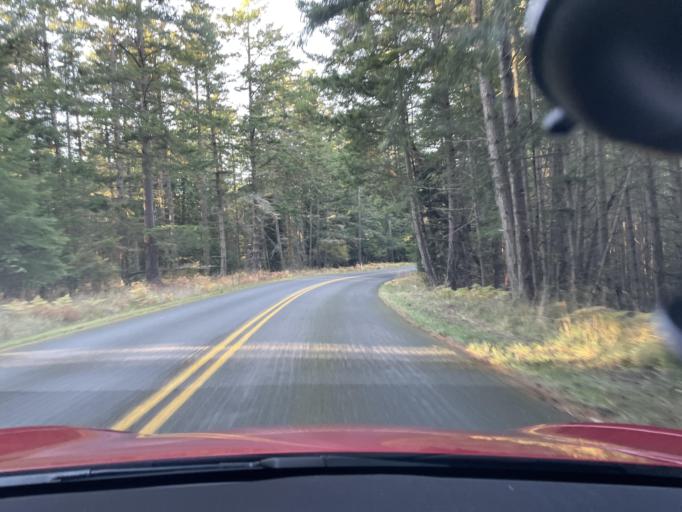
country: US
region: Washington
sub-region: San Juan County
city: Friday Harbor
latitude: 48.5336
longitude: -123.1591
